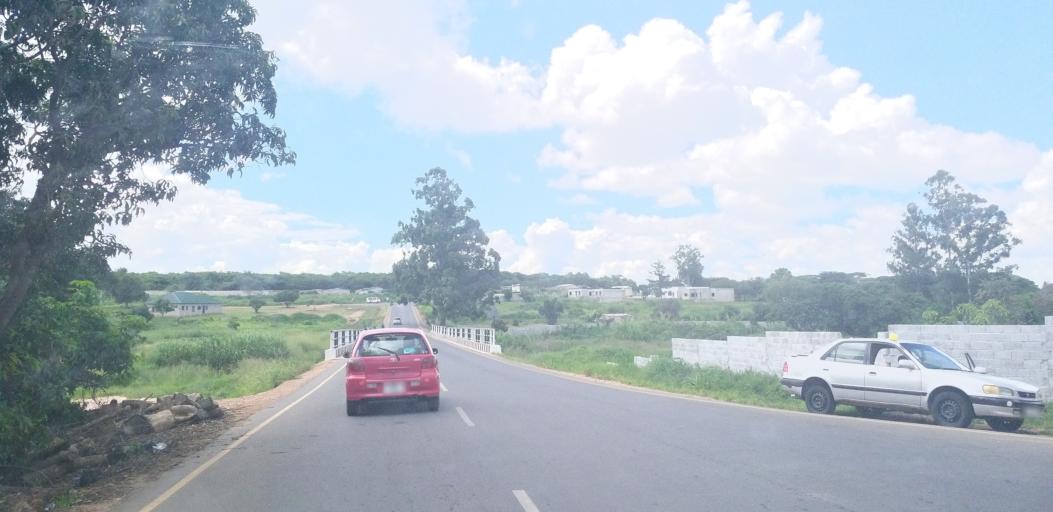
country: ZM
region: Lusaka
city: Lusaka
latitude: -15.3347
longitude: 28.3303
